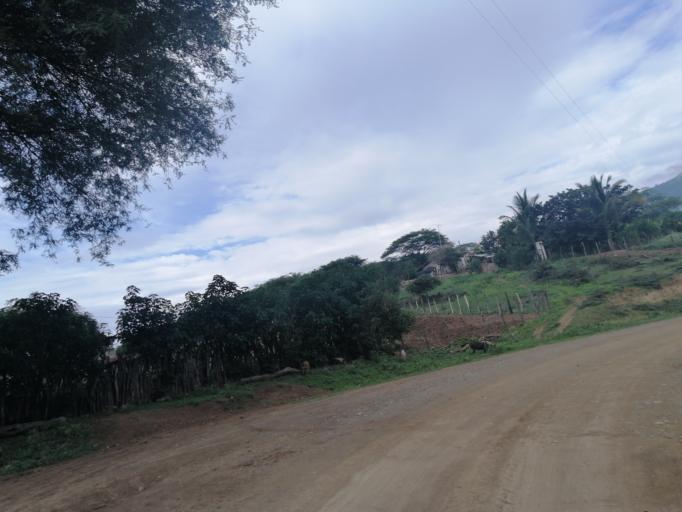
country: EC
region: Loja
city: Catacocha
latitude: -4.0108
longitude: -79.6917
